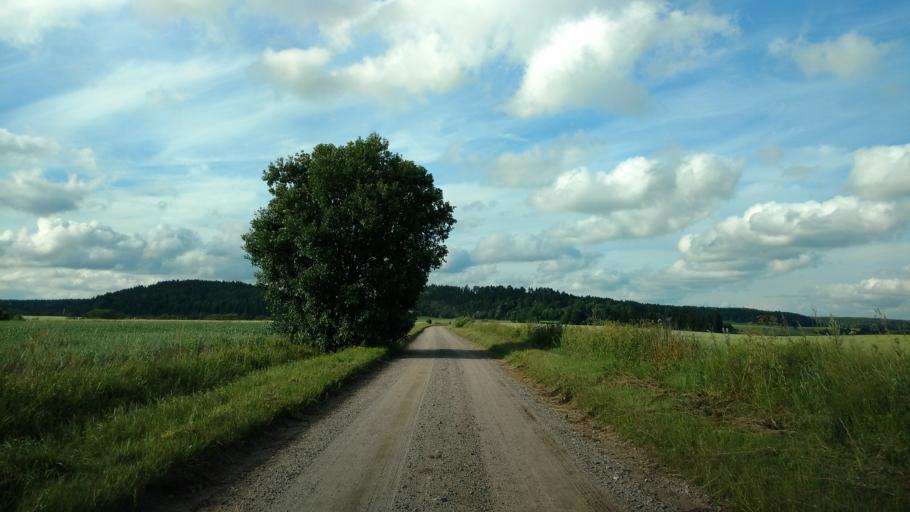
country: FI
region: Varsinais-Suomi
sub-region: Salo
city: Salo
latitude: 60.4175
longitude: 23.1730
